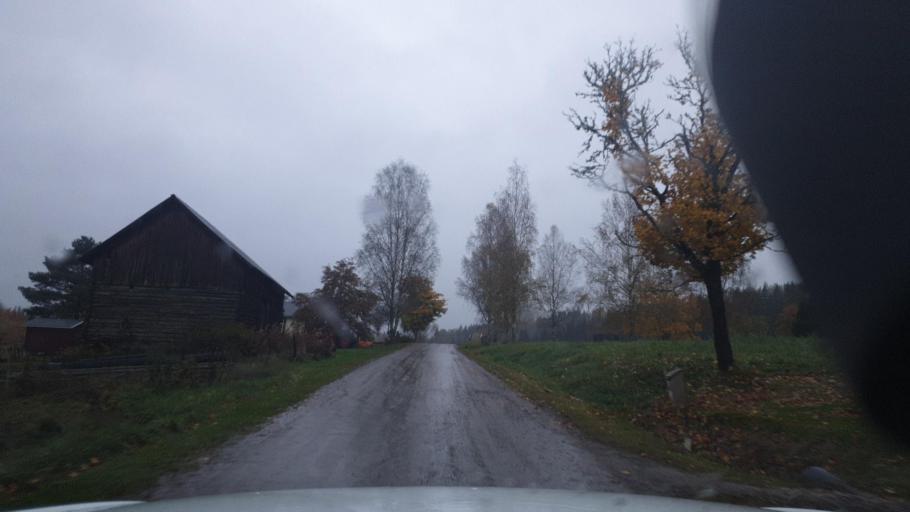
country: SE
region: Vaermland
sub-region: Eda Kommun
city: Amotfors
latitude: 59.7821
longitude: 12.4328
